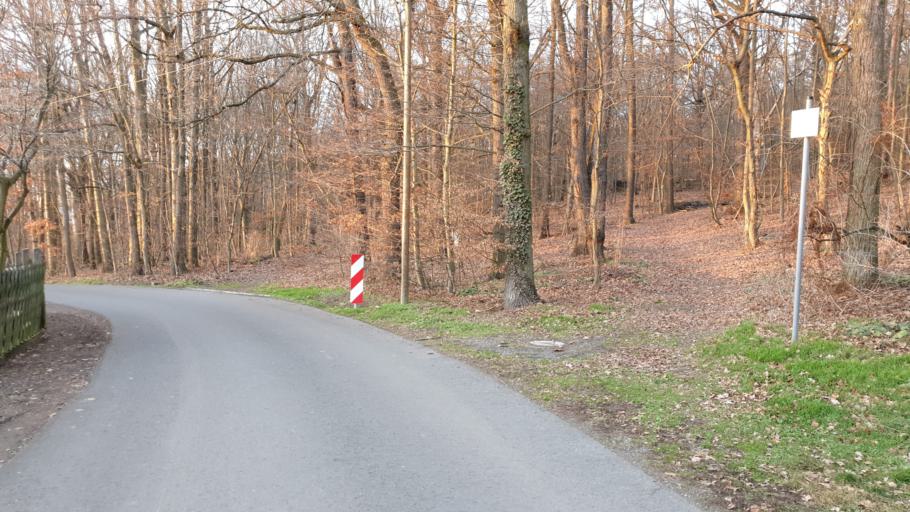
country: DE
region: Saxony
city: Hohburg
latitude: 51.4147
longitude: 12.7950
